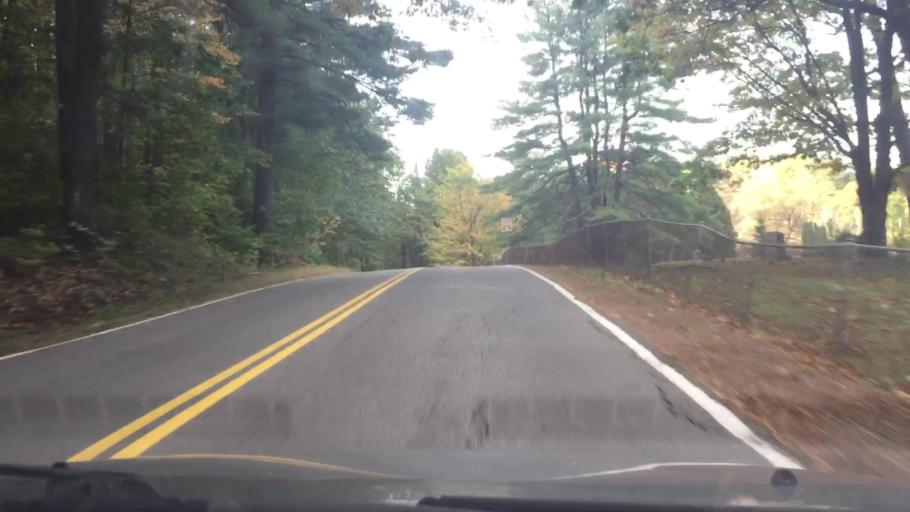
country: US
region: New Hampshire
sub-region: Cheshire County
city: Keene
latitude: 42.9422
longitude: -72.2668
